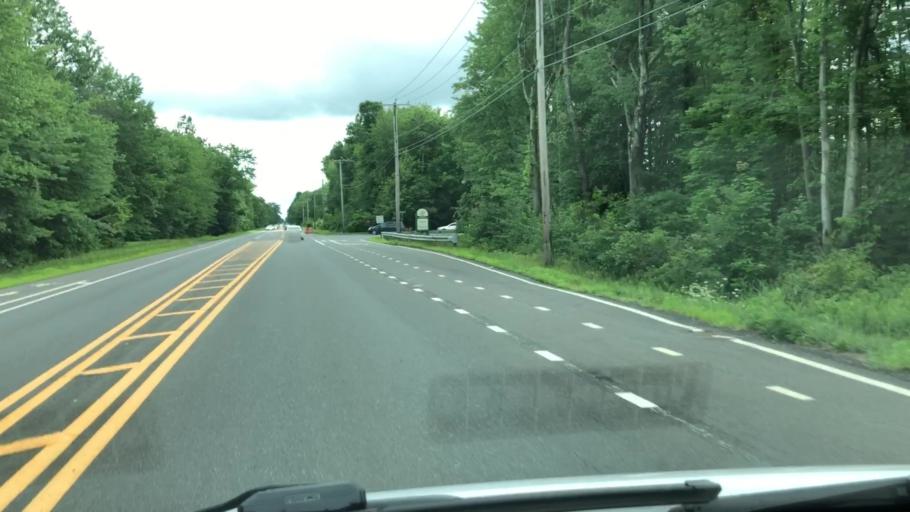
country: US
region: Massachusetts
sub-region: Franklin County
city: South Deerfield
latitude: 42.4953
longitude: -72.6103
